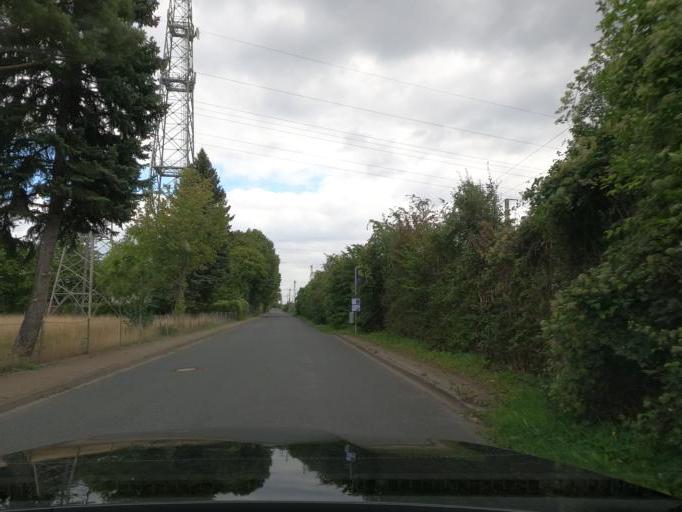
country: DE
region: Lower Saxony
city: Lehrte
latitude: 52.3772
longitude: 9.9149
